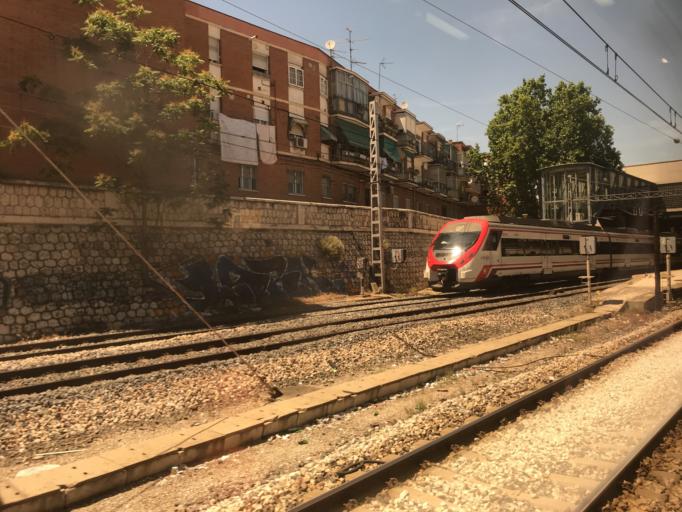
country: ES
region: Madrid
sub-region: Provincia de Madrid
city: Villaverde
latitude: 40.3516
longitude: -3.6841
